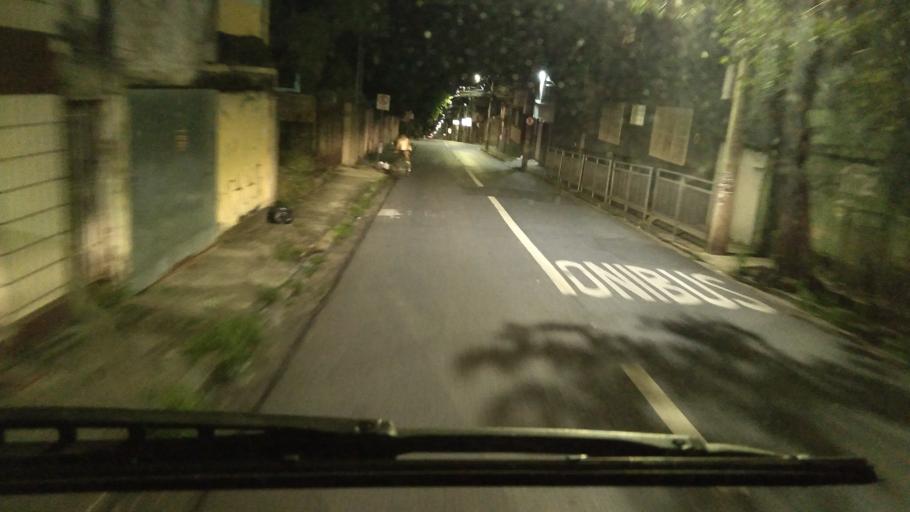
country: BR
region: Minas Gerais
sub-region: Belo Horizonte
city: Belo Horizonte
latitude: -19.9112
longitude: -43.9596
